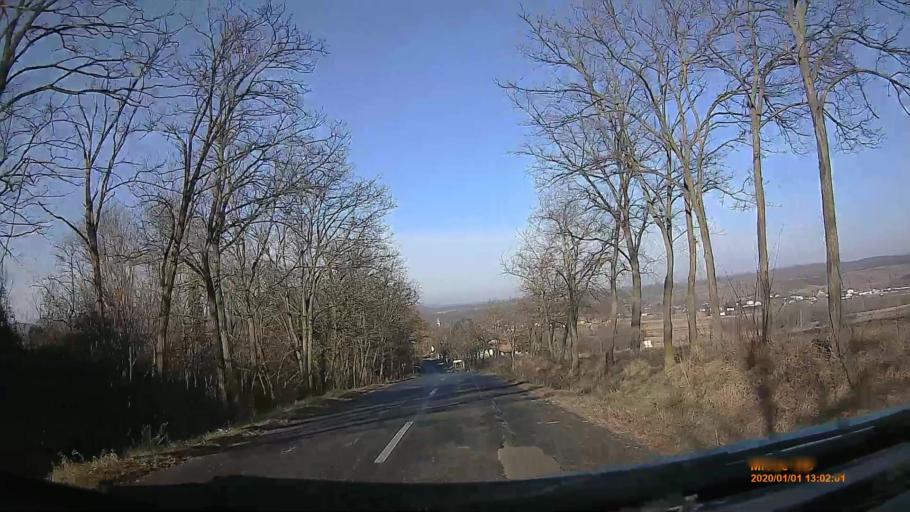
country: HU
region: Heves
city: Parad
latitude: 47.9327
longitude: 20.0252
